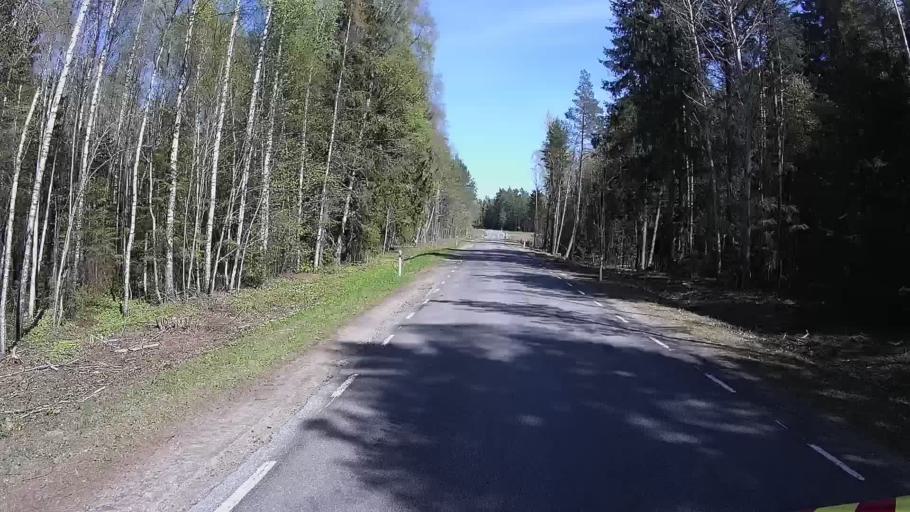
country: EE
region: Harju
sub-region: Nissi vald
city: Turba
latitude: 59.0937
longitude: 23.9954
